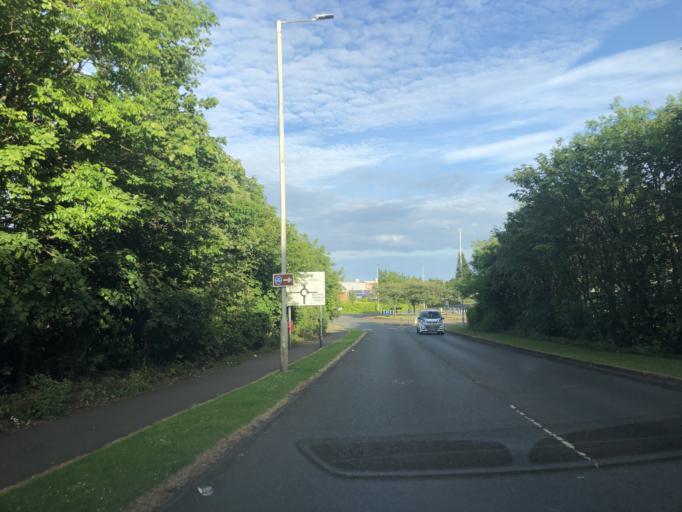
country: GB
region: Scotland
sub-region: Fife
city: Leven
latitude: 56.1967
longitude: -3.0057
